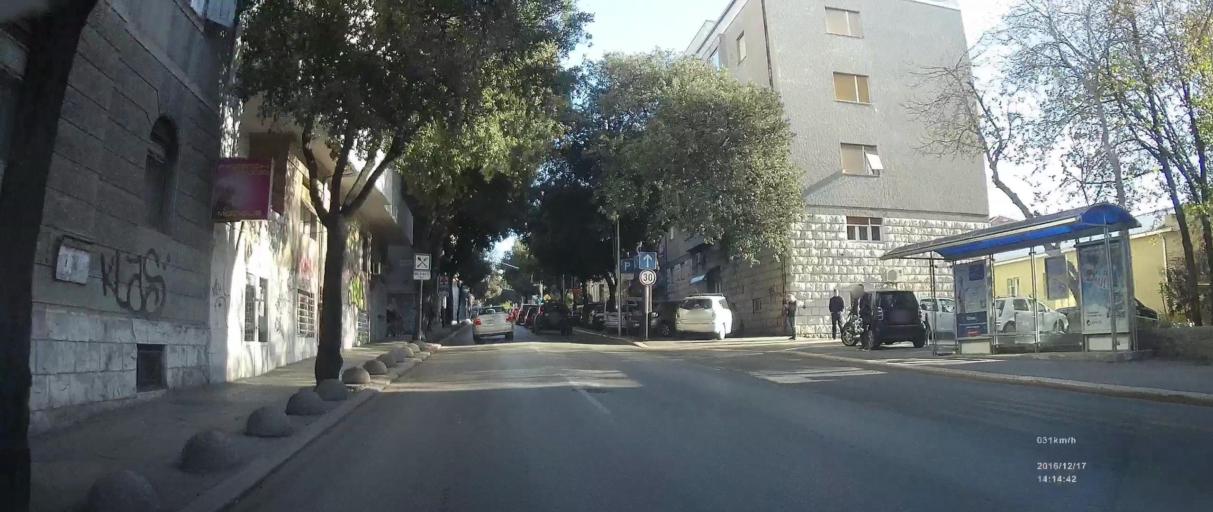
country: HR
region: Splitsko-Dalmatinska
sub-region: Grad Split
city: Split
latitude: 43.5124
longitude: 16.4438
